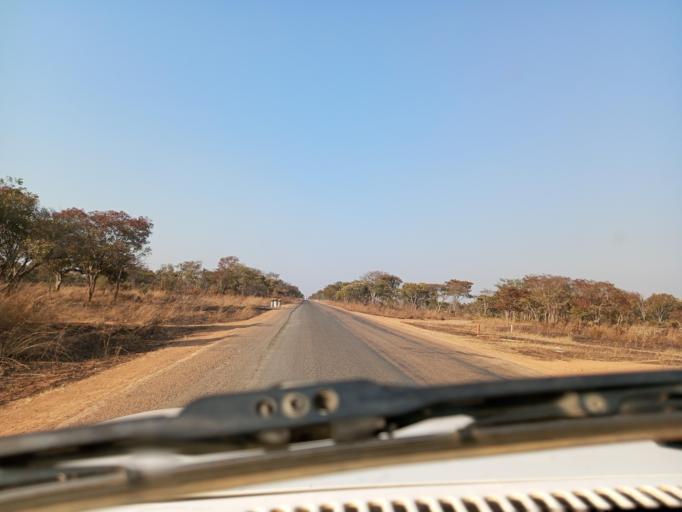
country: ZM
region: Northern
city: Mpika
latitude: -12.4035
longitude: 31.0875
